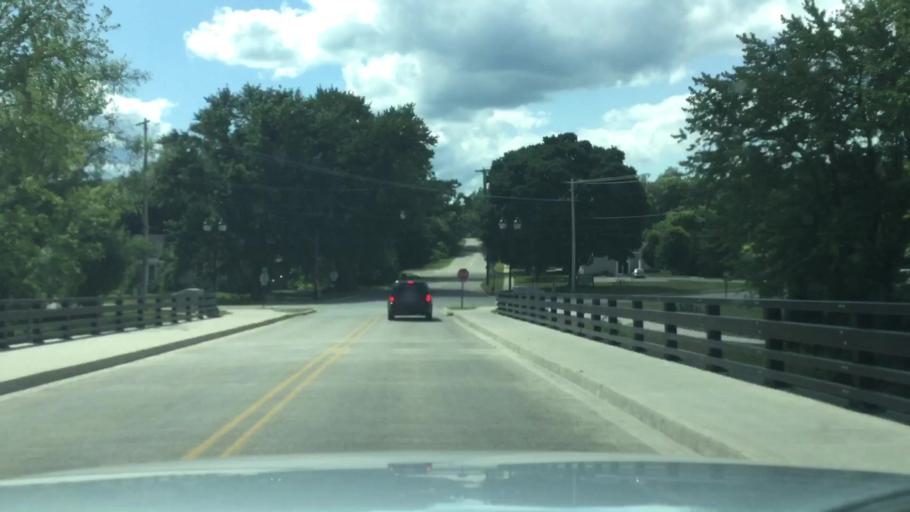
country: US
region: Michigan
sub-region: Ionia County
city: Belding
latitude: 43.0979
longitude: -85.2346
